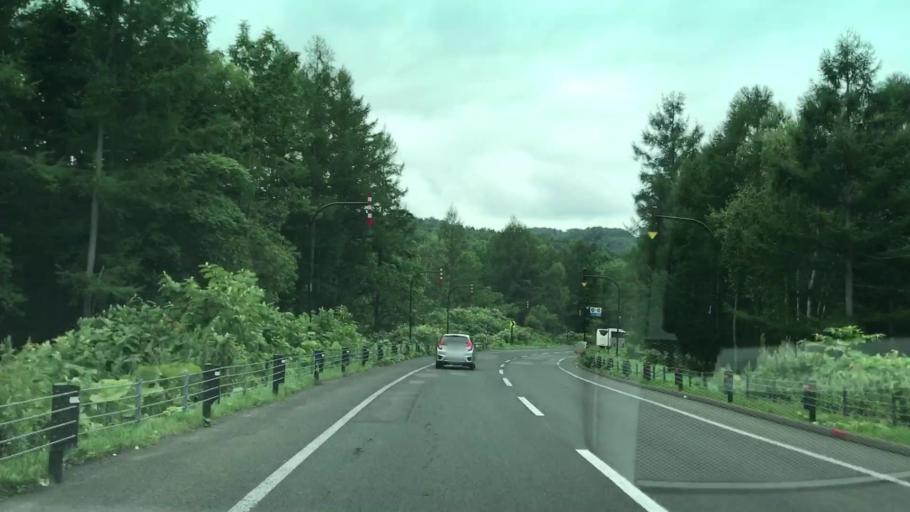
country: JP
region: Hokkaido
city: Niseko Town
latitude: 42.9495
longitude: 140.8525
